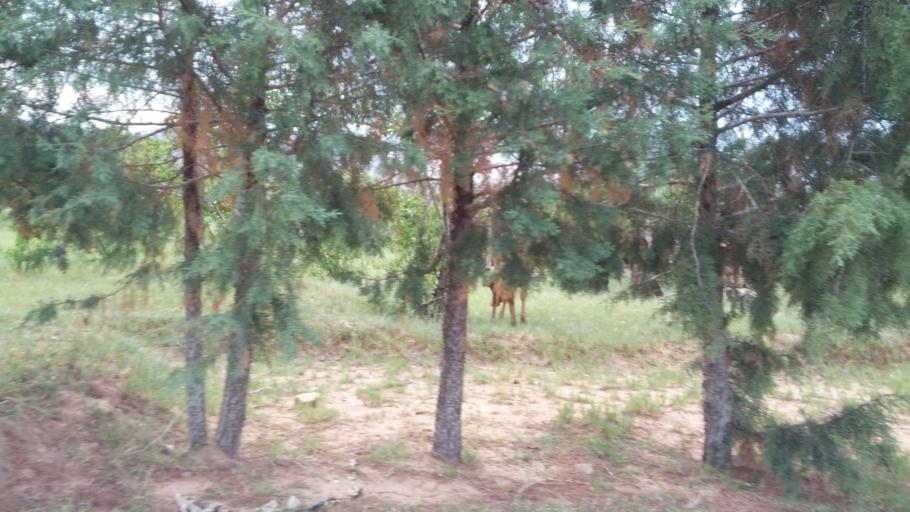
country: LS
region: Mafeteng
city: Mafeteng
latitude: -29.6918
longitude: 27.4321
